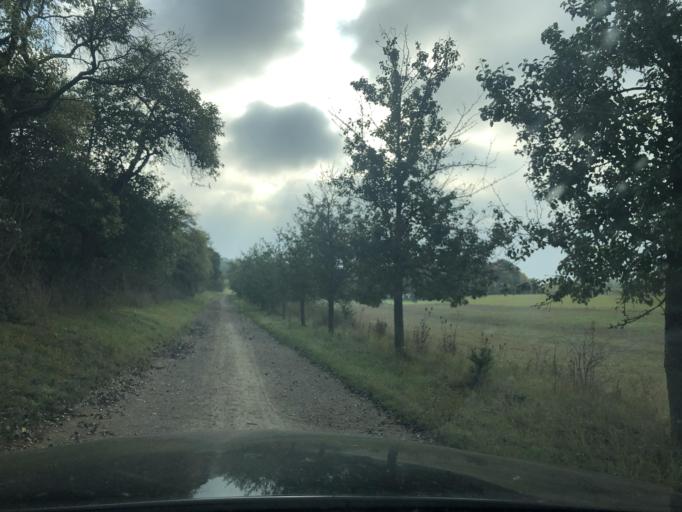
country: DE
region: Thuringia
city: Helmsdorf
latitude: 51.2953
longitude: 10.3889
